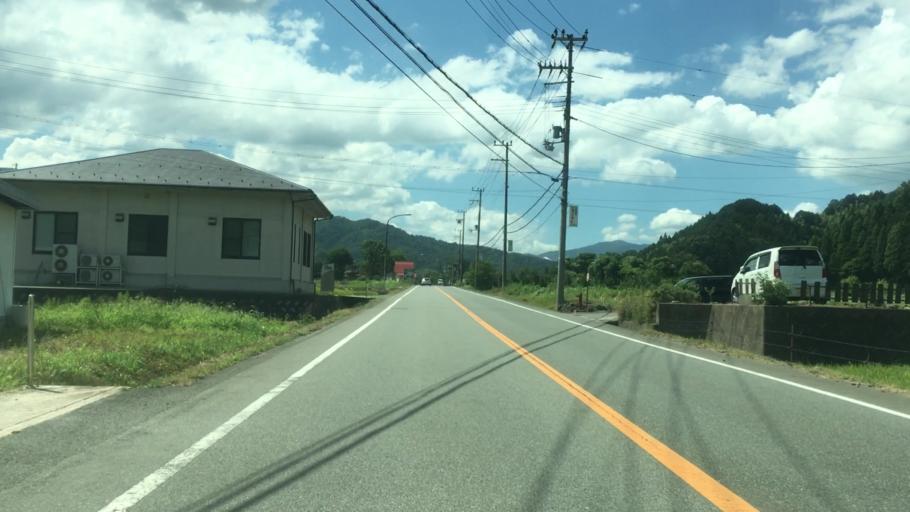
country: JP
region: Hyogo
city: Toyooka
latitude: 35.4645
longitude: 134.7314
